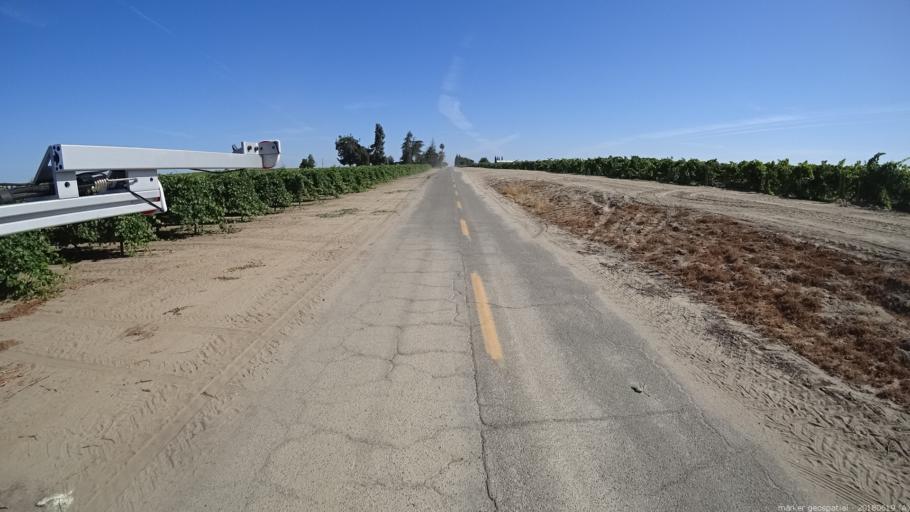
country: US
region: California
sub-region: Fresno County
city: Biola
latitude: 36.8235
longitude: -120.0653
